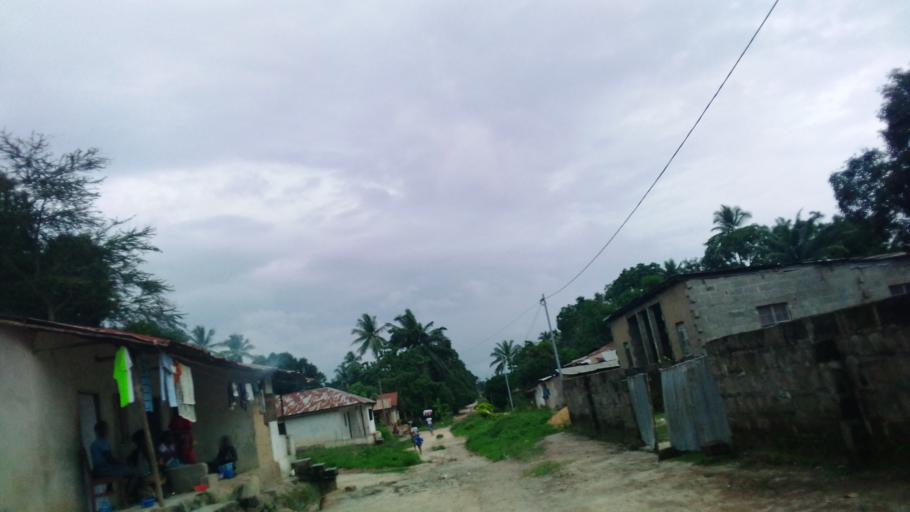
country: SL
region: Northern Province
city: Lunsar
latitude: 8.6862
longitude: -12.5405
